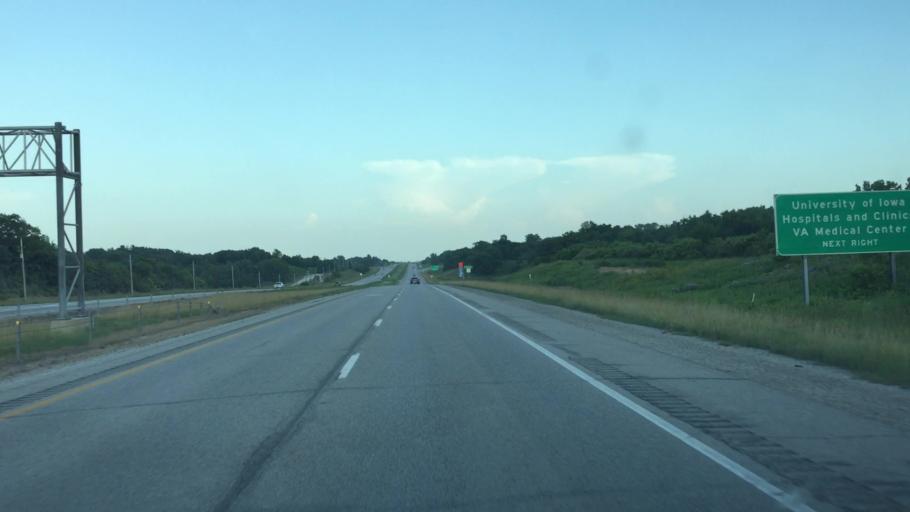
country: US
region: Iowa
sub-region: Johnson County
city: Coralville
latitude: 41.6663
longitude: -91.6110
